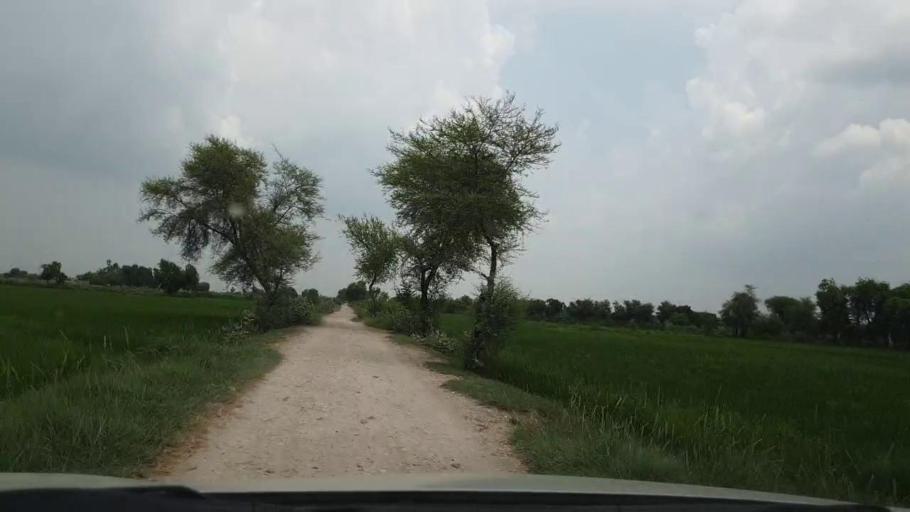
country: PK
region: Sindh
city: Goth Garelo
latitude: 27.4283
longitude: 68.0838
